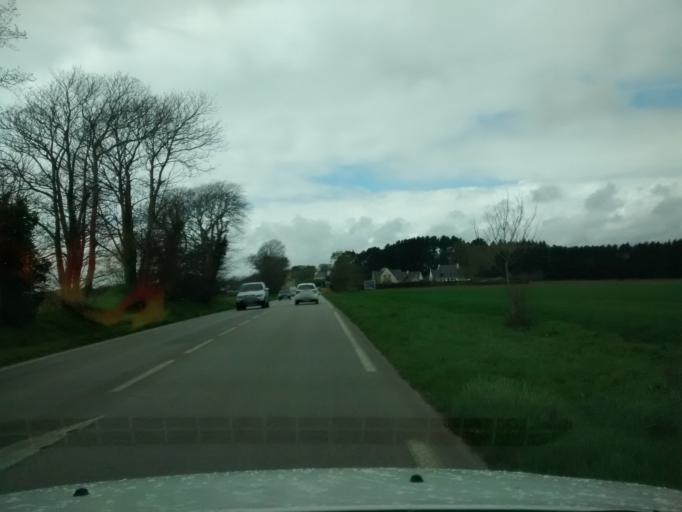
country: FR
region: Brittany
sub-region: Departement du Morbihan
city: Queven
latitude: 47.7735
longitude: -3.4139
